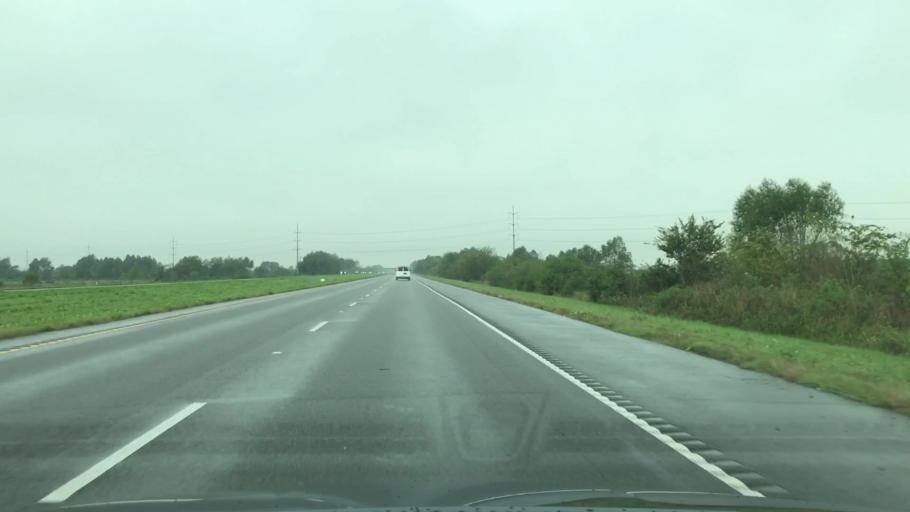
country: US
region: Louisiana
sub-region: Lafourche Parish
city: Raceland
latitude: 29.6901
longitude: -90.6083
